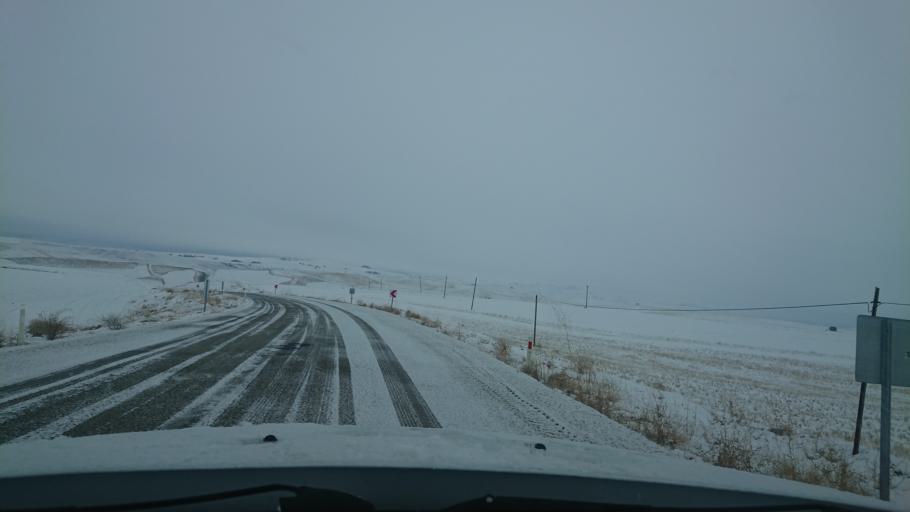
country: TR
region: Aksaray
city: Agacoren
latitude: 38.7809
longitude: 33.8720
